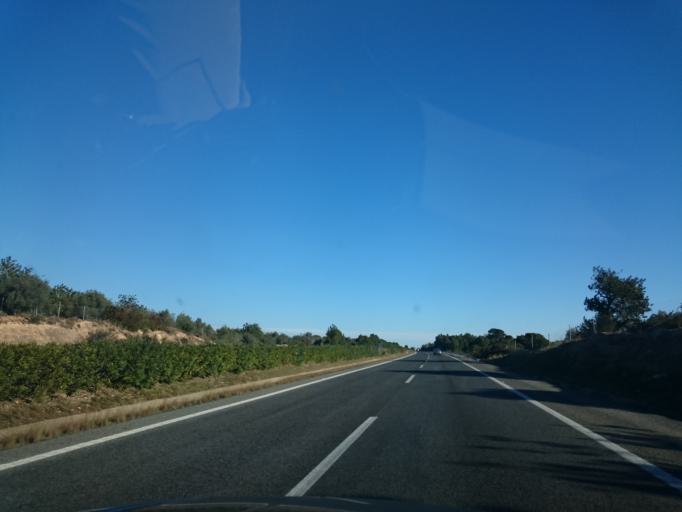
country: ES
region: Catalonia
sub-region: Provincia de Tarragona
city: L'Ampolla
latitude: 40.8215
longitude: 0.7229
